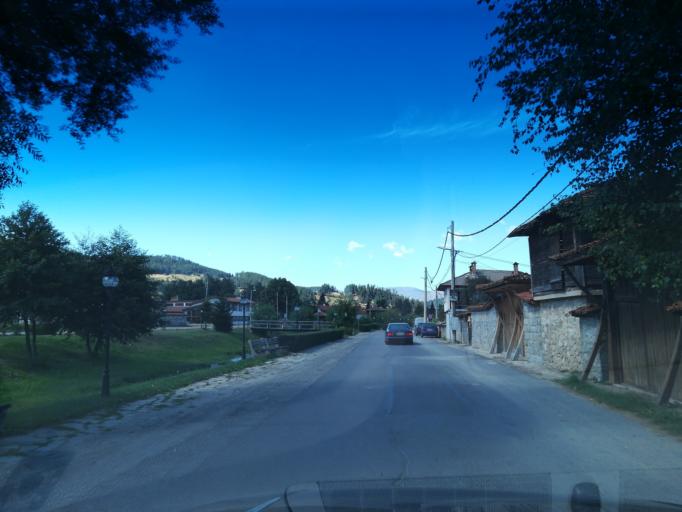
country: BG
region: Sofiya
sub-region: Obshtina Koprivshtitsa
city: Koprivshtitsa
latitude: 42.6324
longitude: 24.3624
